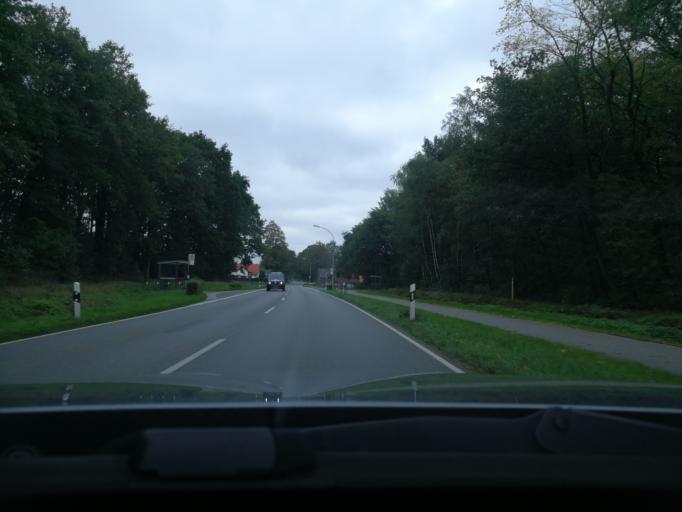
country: DE
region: North Rhine-Westphalia
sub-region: Regierungsbezirk Dusseldorf
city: Kevelaer
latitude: 51.5163
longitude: 6.2436
